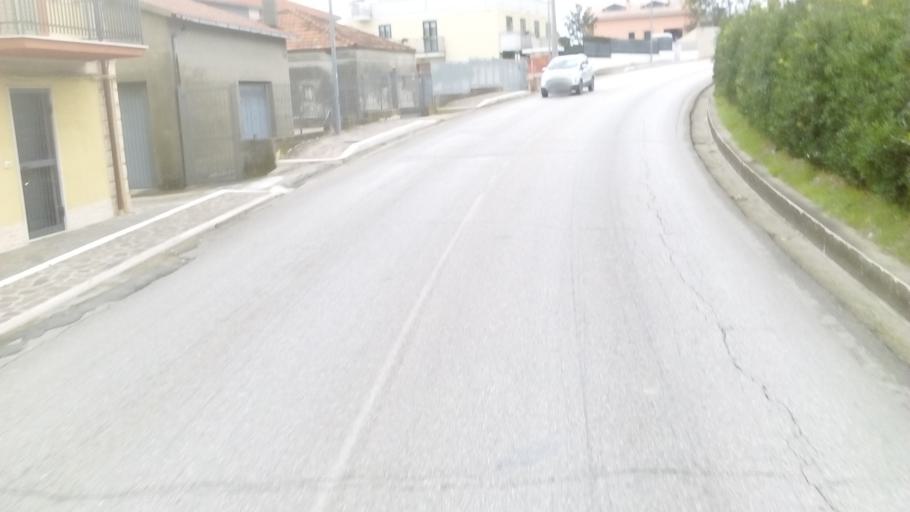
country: IT
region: Abruzzo
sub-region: Provincia di Chieti
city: Vasto
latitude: 42.0967
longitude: 14.6966
